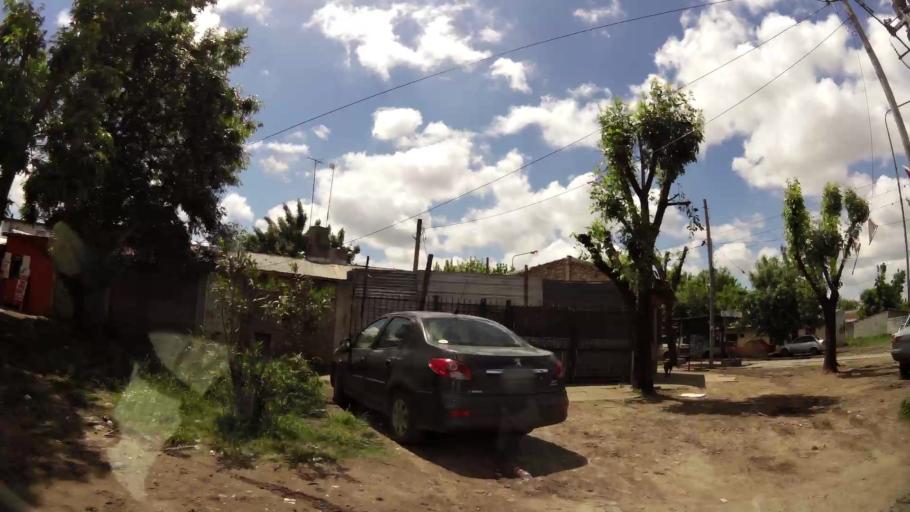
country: AR
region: Buenos Aires
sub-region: Partido de Quilmes
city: Quilmes
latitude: -34.8373
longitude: -58.2380
